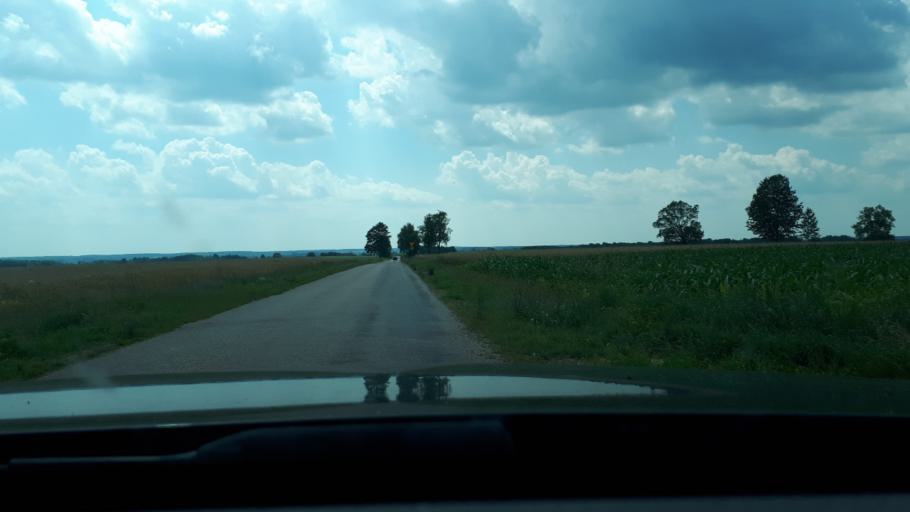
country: PL
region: Podlasie
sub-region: Powiat bialostocki
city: Lapy
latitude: 53.0967
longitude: 22.8584
